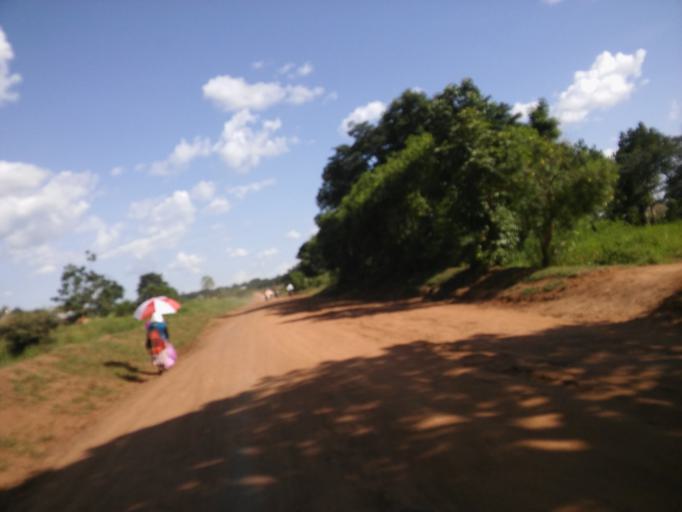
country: UG
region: Eastern Region
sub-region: Kibuku District
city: Kibuku
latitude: 1.0670
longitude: 33.7550
